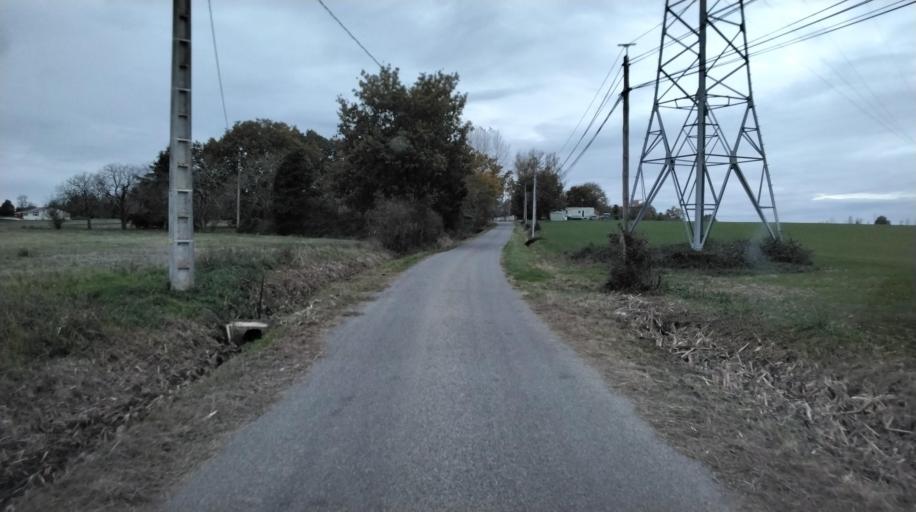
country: FR
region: Midi-Pyrenees
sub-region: Departement de la Haute-Garonne
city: Berat
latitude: 43.3903
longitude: 1.1996
